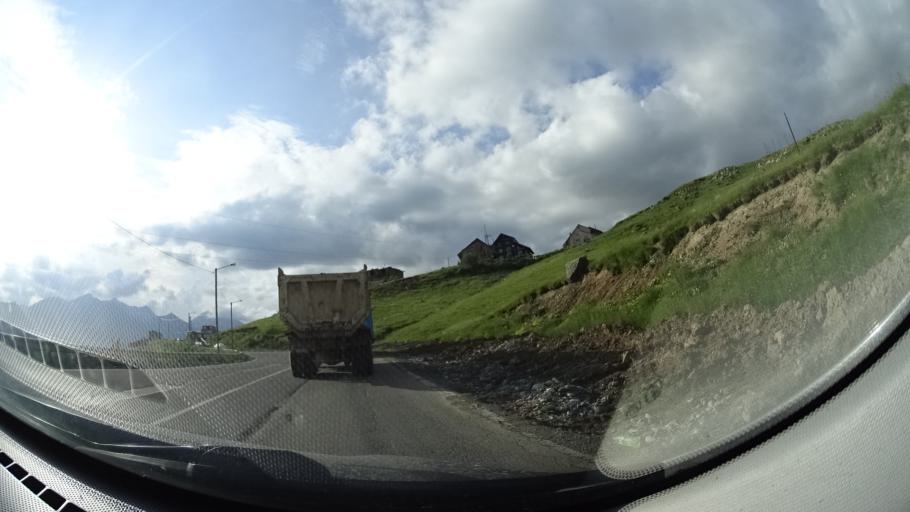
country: GE
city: Gudauri
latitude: 42.4747
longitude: 44.4805
